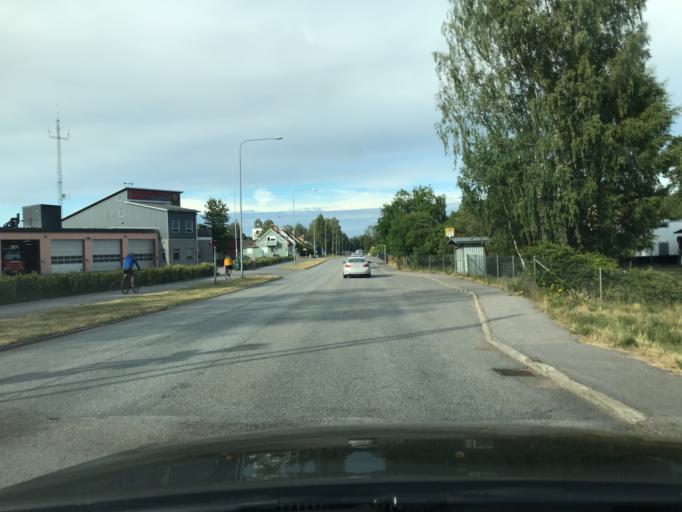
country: SE
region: Kalmar
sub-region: Hultsfreds Kommun
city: Hultsfred
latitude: 57.4928
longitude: 15.8426
